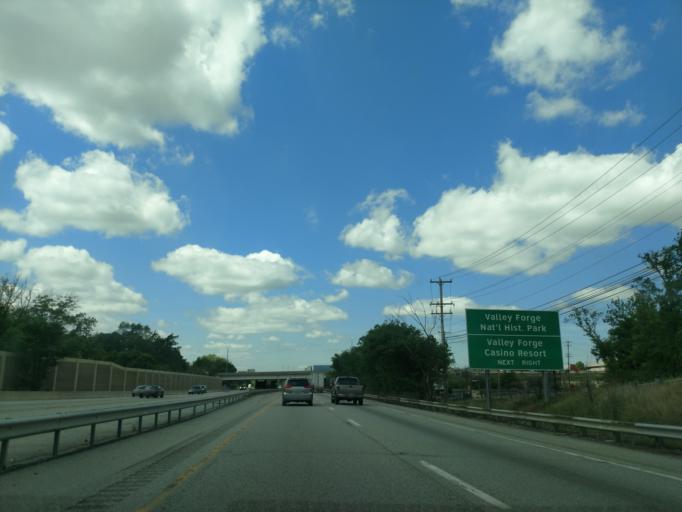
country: US
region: Pennsylvania
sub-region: Montgomery County
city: King of Prussia
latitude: 40.0882
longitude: -75.4133
